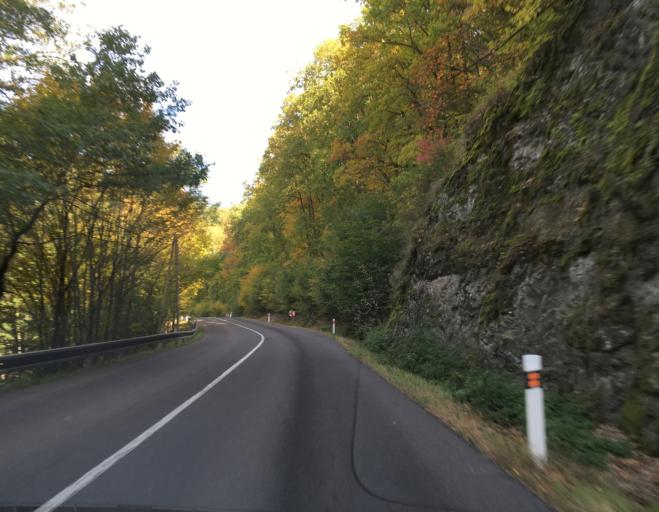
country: SK
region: Banskobystricky
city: Krupina
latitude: 48.3055
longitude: 18.9752
